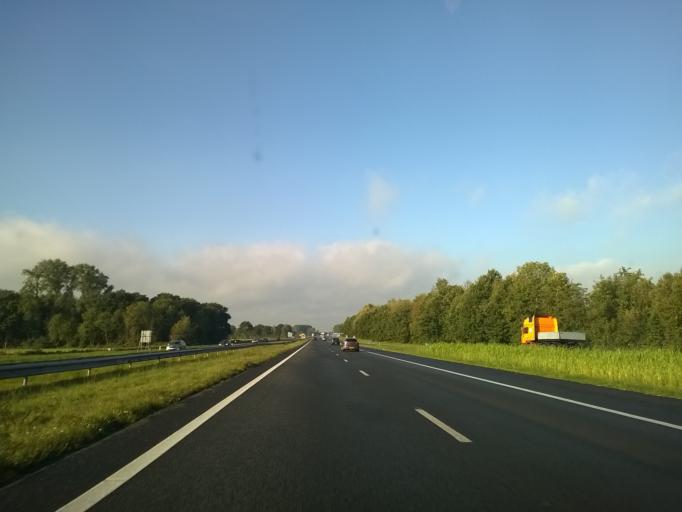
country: NL
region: Groningen
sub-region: Gemeente Leek
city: Leek
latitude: 53.1696
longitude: 6.3266
